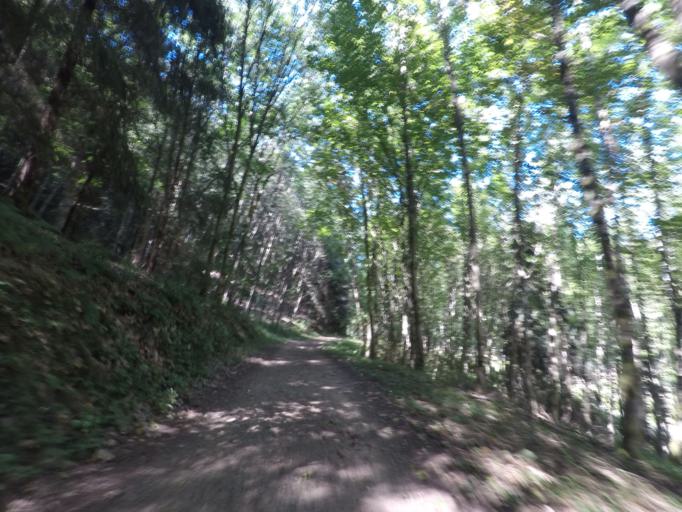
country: LU
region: Luxembourg
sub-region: Canton de Luxembourg
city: Strassen
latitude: 49.6279
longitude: 6.0958
